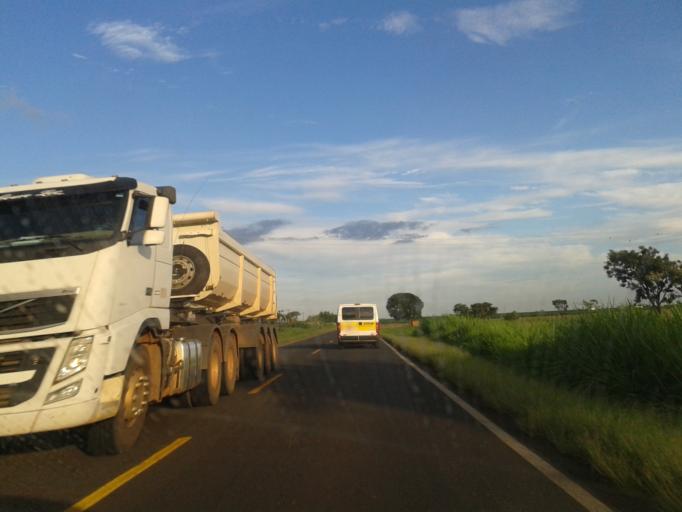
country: BR
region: Minas Gerais
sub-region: Araguari
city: Araguari
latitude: -18.6363
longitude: -48.2271
